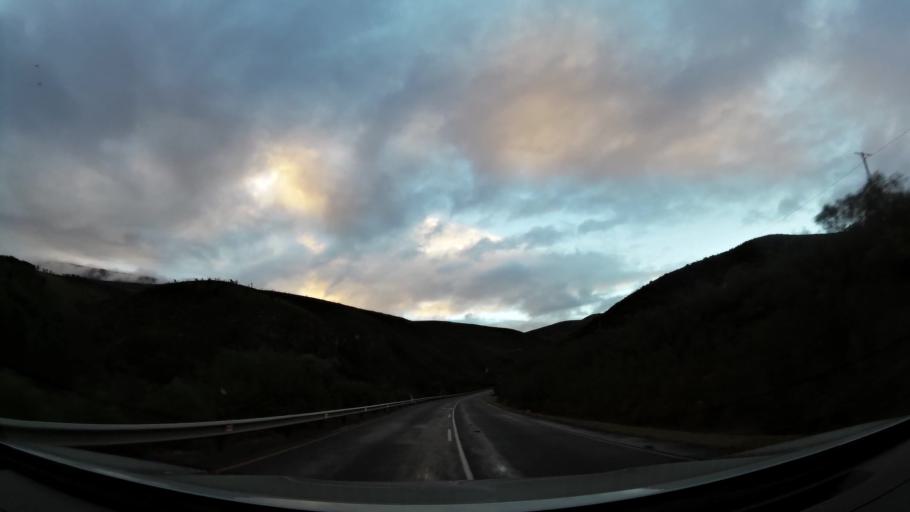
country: ZA
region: Western Cape
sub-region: Overberg District Municipality
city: Swellendam
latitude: -33.9961
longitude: 20.7046
